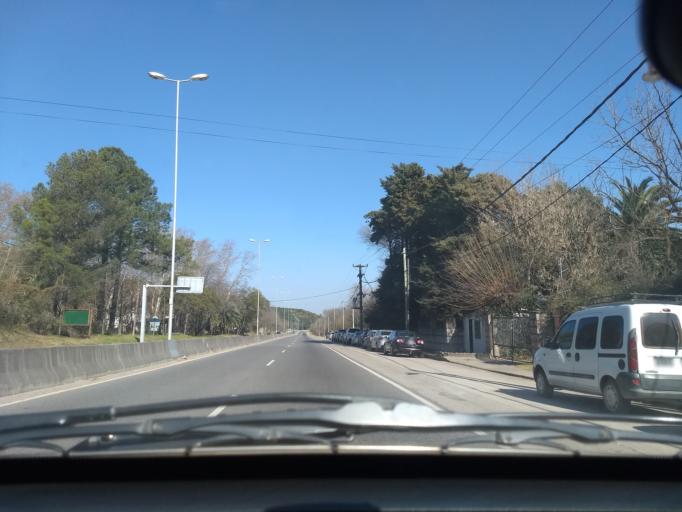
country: AR
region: Cordoba
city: Rio Ceballos
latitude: -31.1620
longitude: -64.3014
